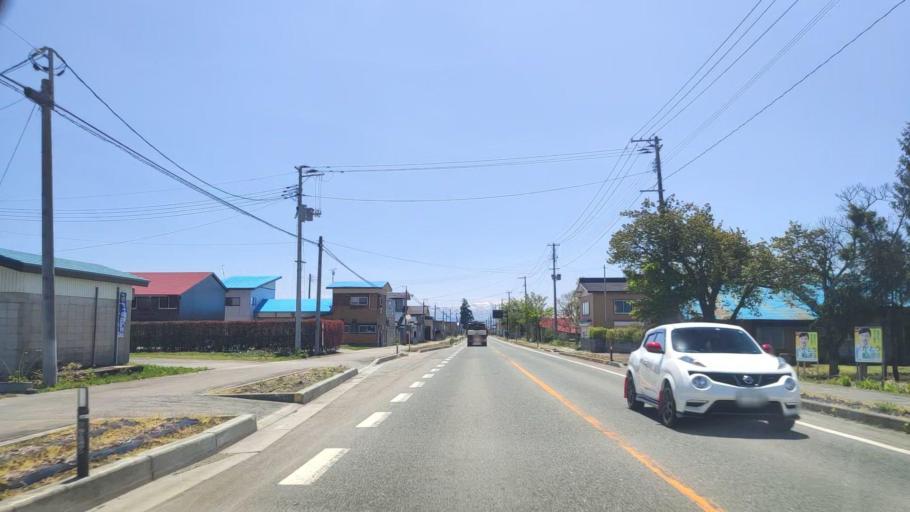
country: JP
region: Yamagata
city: Shinjo
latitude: 38.8174
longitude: 140.3255
